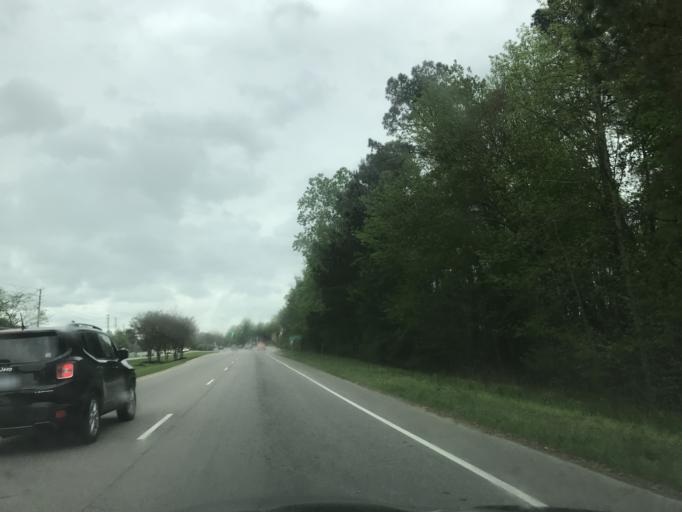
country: US
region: North Carolina
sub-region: Wake County
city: Knightdale
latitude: 35.7988
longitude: -78.4772
